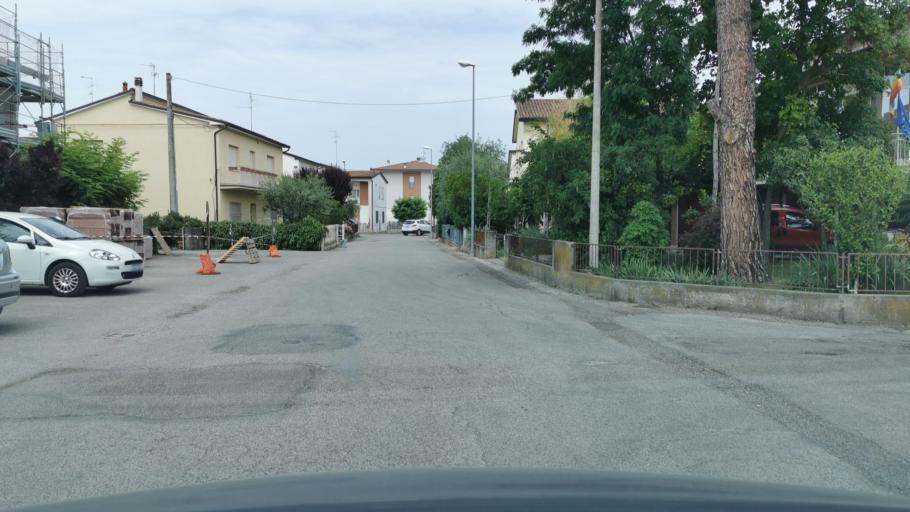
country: IT
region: Emilia-Romagna
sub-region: Provincia di Ravenna
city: Bagnacavallo
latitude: 44.4142
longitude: 11.9700
